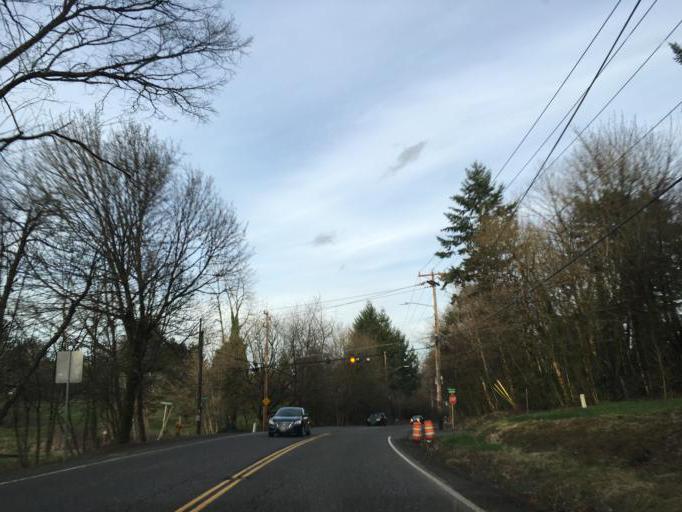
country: US
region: Oregon
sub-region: Clackamas County
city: Lake Oswego
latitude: 45.4358
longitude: -122.6979
